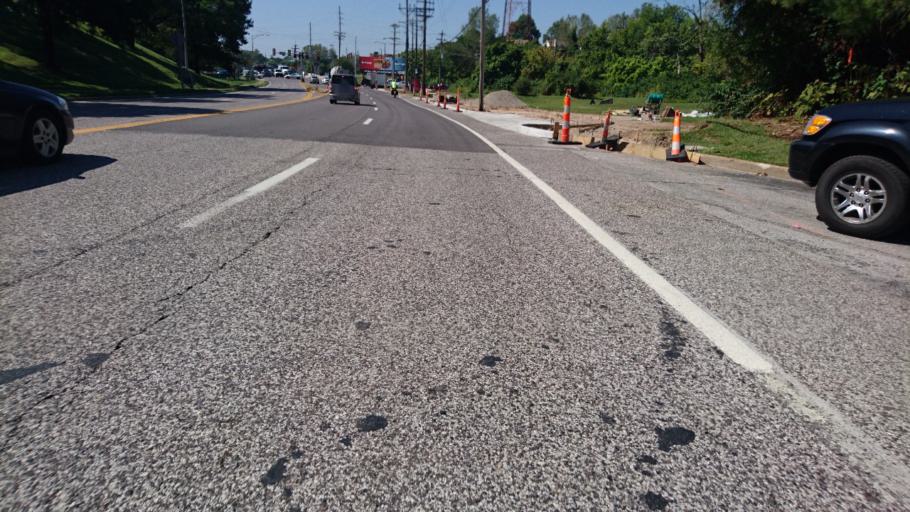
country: US
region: Missouri
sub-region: Saint Louis County
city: Maplewood
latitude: 38.6135
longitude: -90.3319
